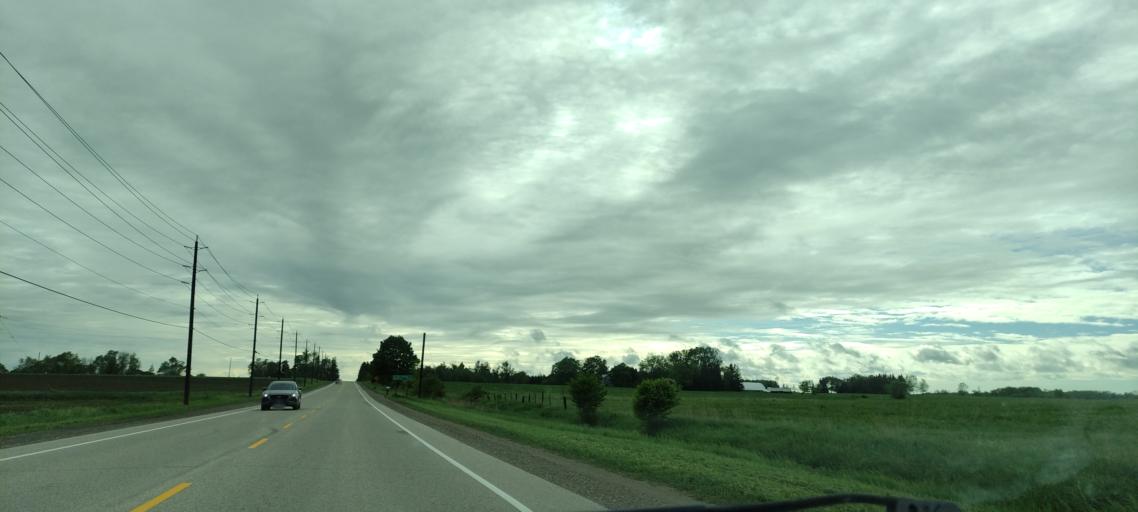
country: CA
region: Ontario
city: Kitchener
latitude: 43.3794
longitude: -80.6684
